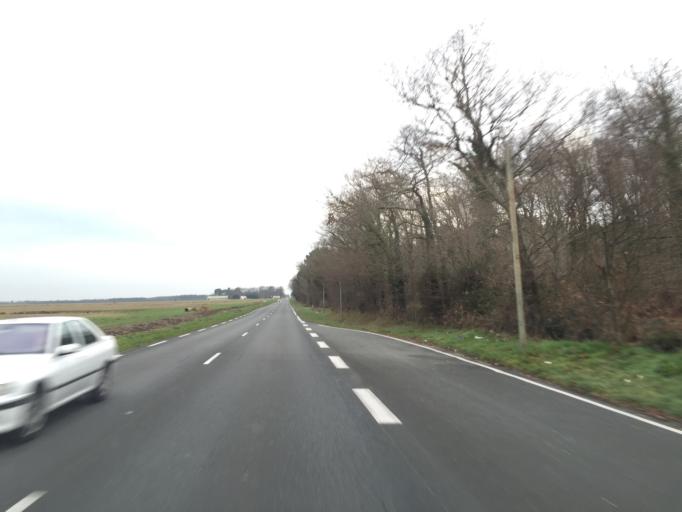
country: FR
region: Aquitaine
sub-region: Departement de la Gironde
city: Saint-Sauveur
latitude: 45.1987
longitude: -0.8574
